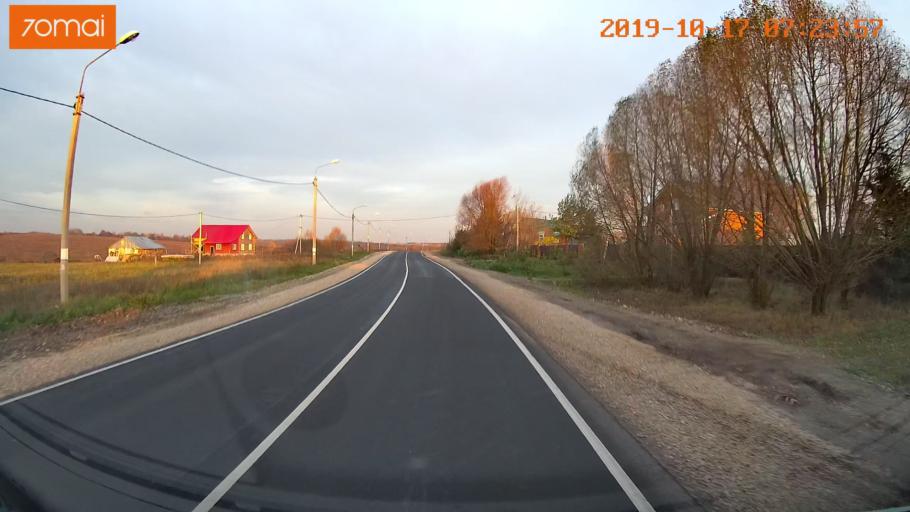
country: RU
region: Vladimir
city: Stavrovo
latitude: 56.3333
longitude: 40.1149
